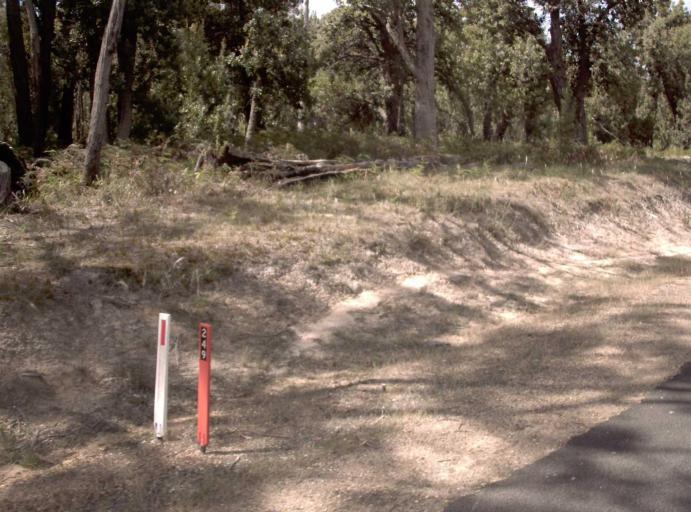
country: AU
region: Victoria
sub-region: Wellington
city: Sale
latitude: -37.9177
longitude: 147.2890
